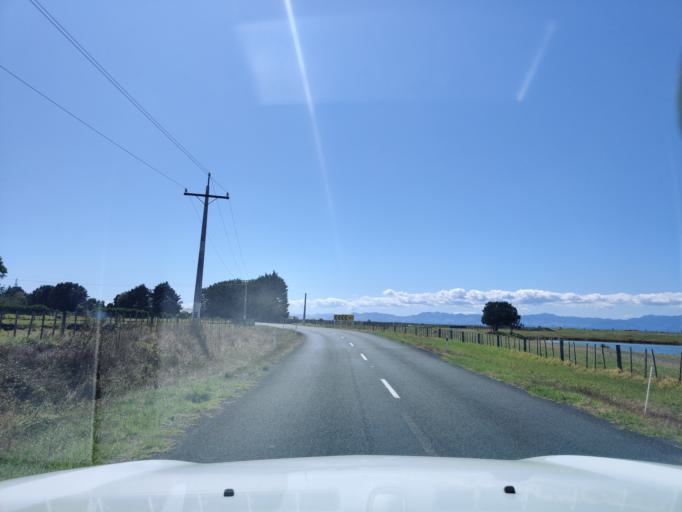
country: NZ
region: Waikato
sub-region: Thames-Coromandel District
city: Thames
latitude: -37.0557
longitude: 175.3014
